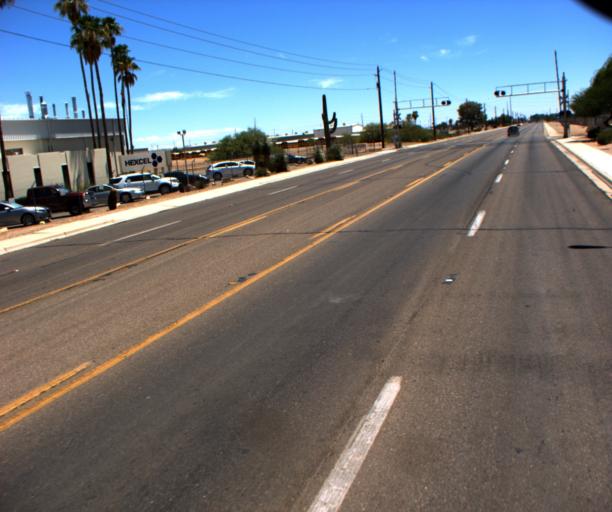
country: US
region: Arizona
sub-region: Pinal County
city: Casa Grande
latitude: 32.8794
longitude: -111.7839
